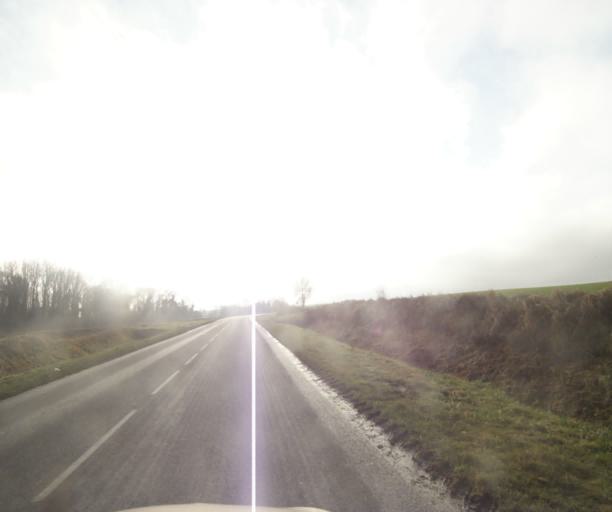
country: FR
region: Nord-Pas-de-Calais
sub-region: Departement du Nord
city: Thiant
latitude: 50.2751
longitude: 3.4541
